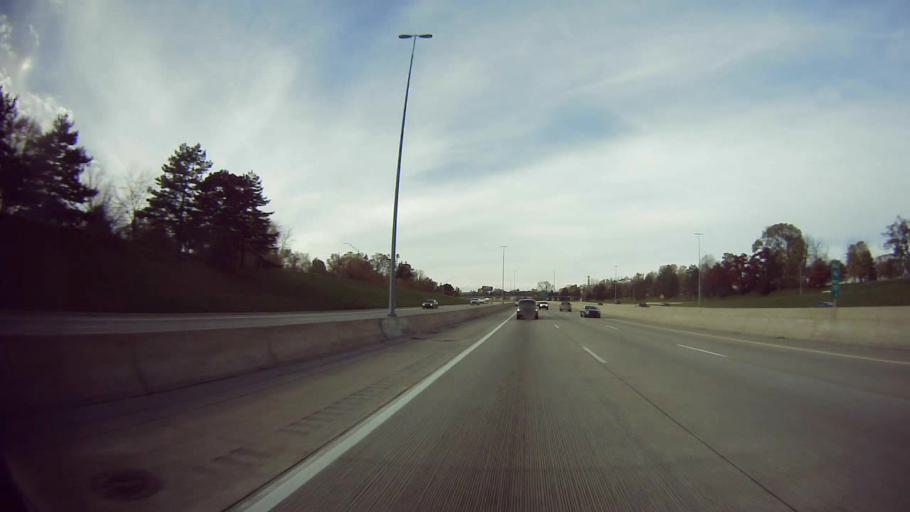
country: US
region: Michigan
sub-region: Wayne County
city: Dearborn Heights
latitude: 42.3822
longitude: -83.2391
